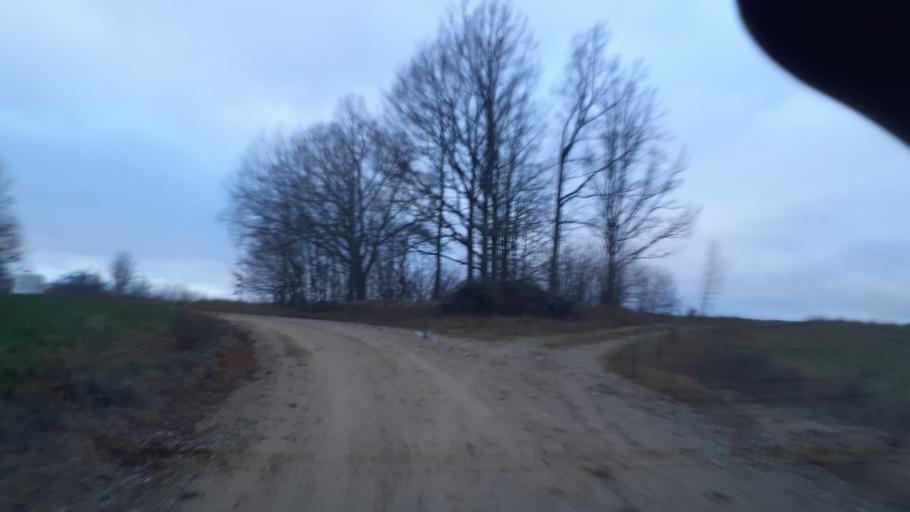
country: LV
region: Alsunga
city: Alsunga
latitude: 56.8938
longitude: 21.6245
